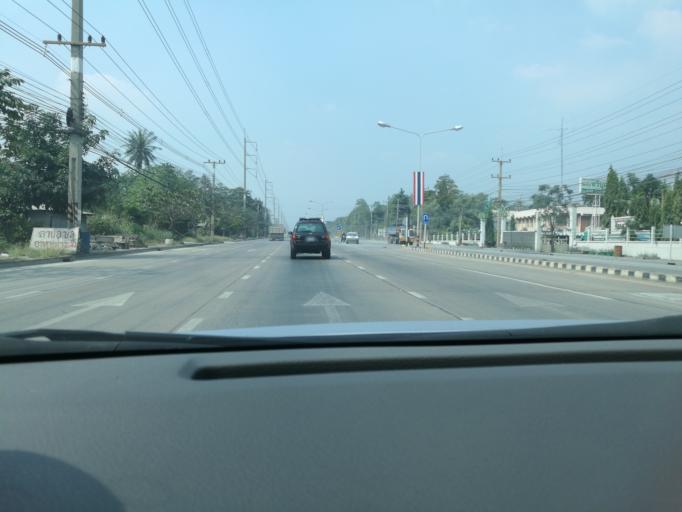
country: TH
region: Sara Buri
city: Phra Phutthabat
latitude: 14.7000
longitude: 100.8592
